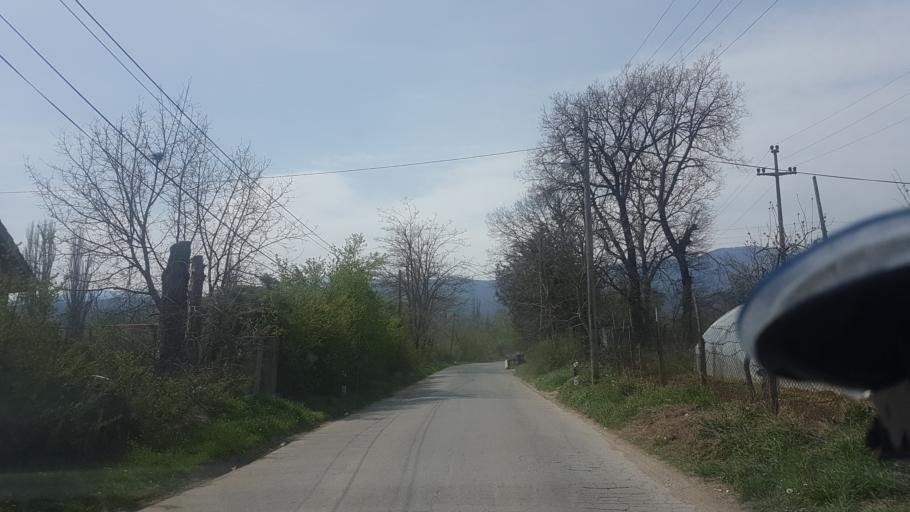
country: MK
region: Zelenikovo
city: Zelenikovo
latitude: 41.8961
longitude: 21.6028
